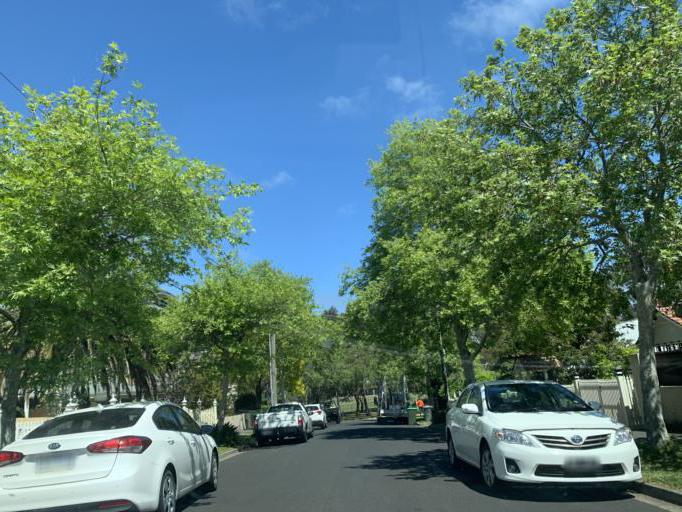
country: AU
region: Victoria
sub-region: Bayside
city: Brighton East
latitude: -37.9090
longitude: 145.0144
